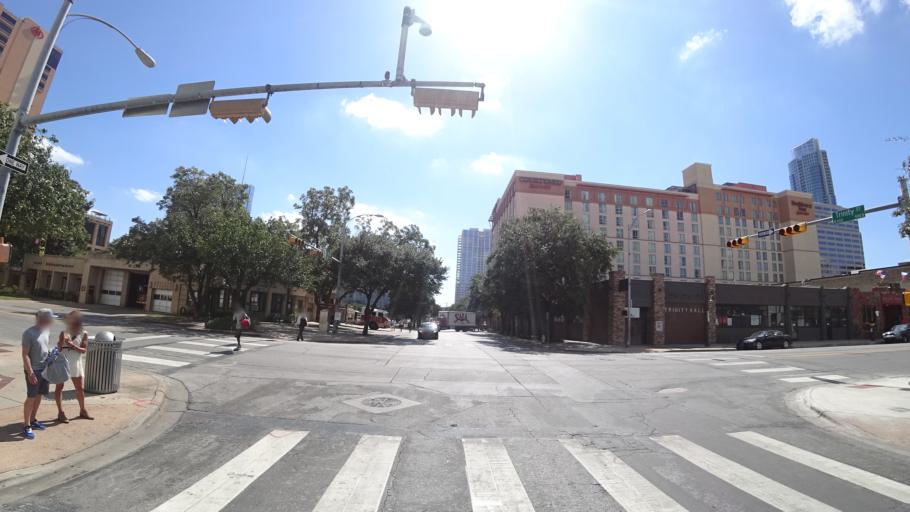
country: US
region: Texas
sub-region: Travis County
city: Austin
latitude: 30.2663
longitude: -97.7396
